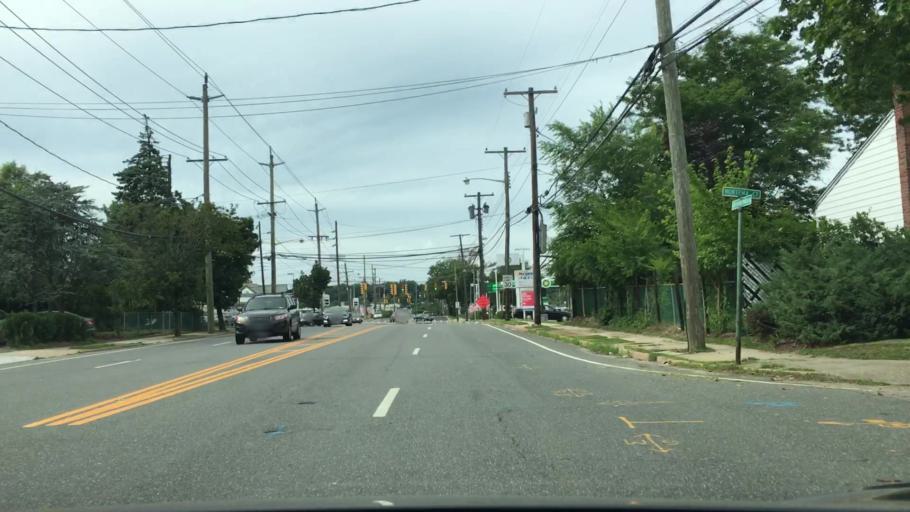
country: US
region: New York
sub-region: Nassau County
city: Manhasset Hills
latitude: 40.7535
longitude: -73.6873
